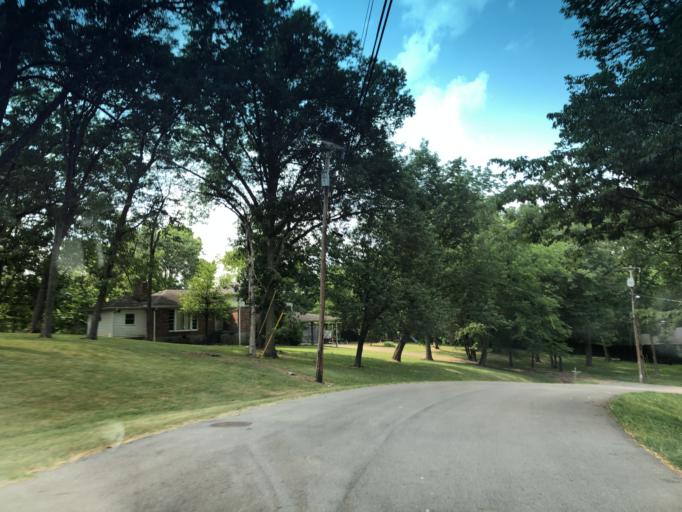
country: US
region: Tennessee
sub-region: Davidson County
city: Goodlettsville
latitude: 36.2689
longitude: -86.7313
